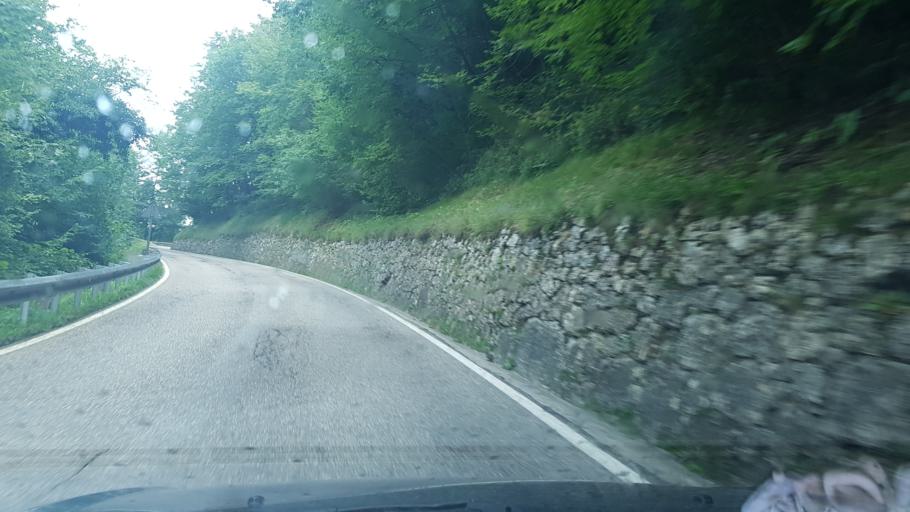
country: IT
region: Veneto
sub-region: Provincia di Vicenza
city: Recoaro Terme
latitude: 45.7629
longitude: 11.1940
